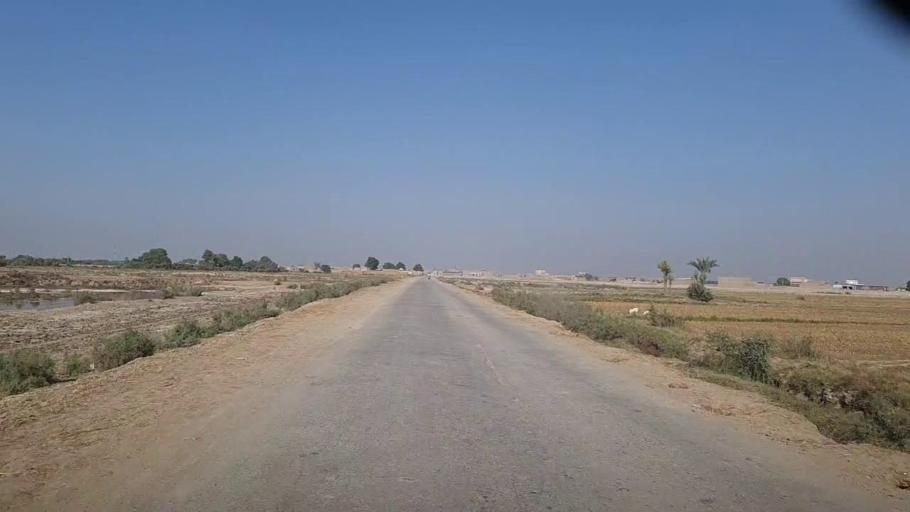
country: PK
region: Sindh
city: Tangwani
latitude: 28.2580
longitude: 68.9974
